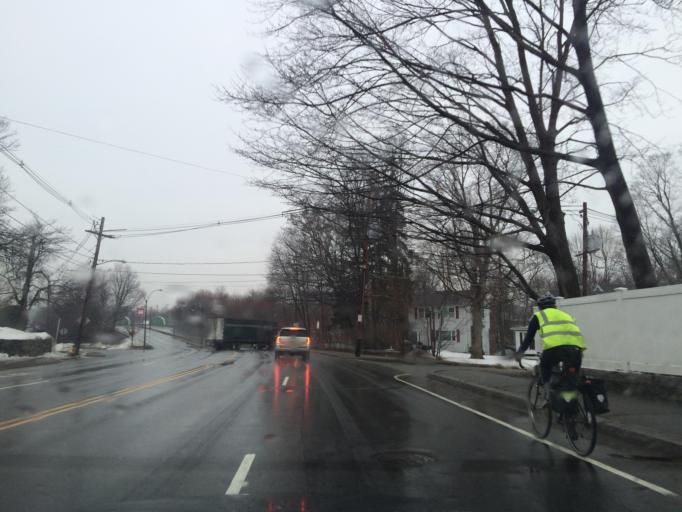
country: US
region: Massachusetts
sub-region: Middlesex County
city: Waltham
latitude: 42.3777
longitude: -71.2203
